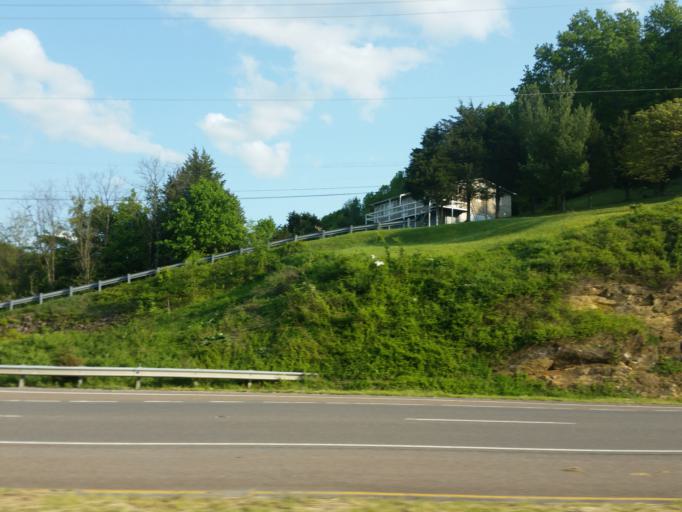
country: US
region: Virginia
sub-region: Tazewell County
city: Claypool Hill
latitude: 37.0412
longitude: -81.7905
